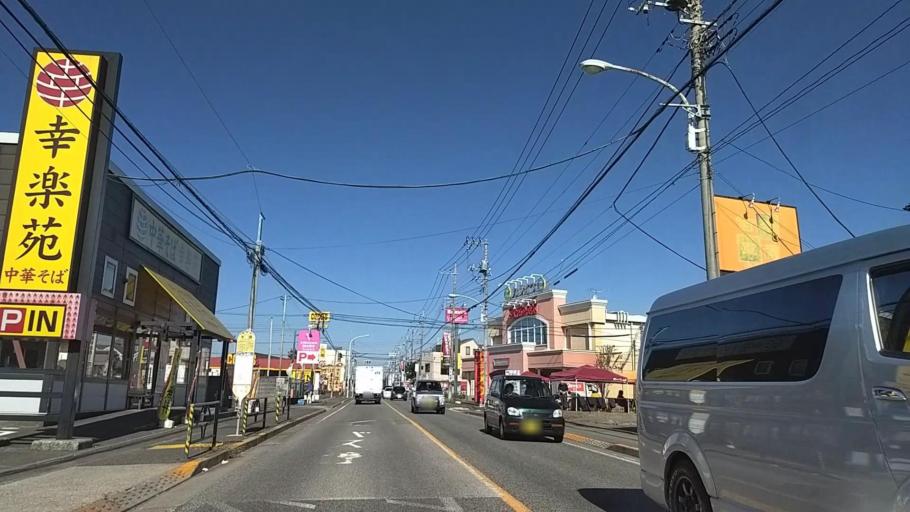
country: JP
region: Tokyo
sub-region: Machida-shi
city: Machida
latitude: 35.5684
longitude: 139.4226
